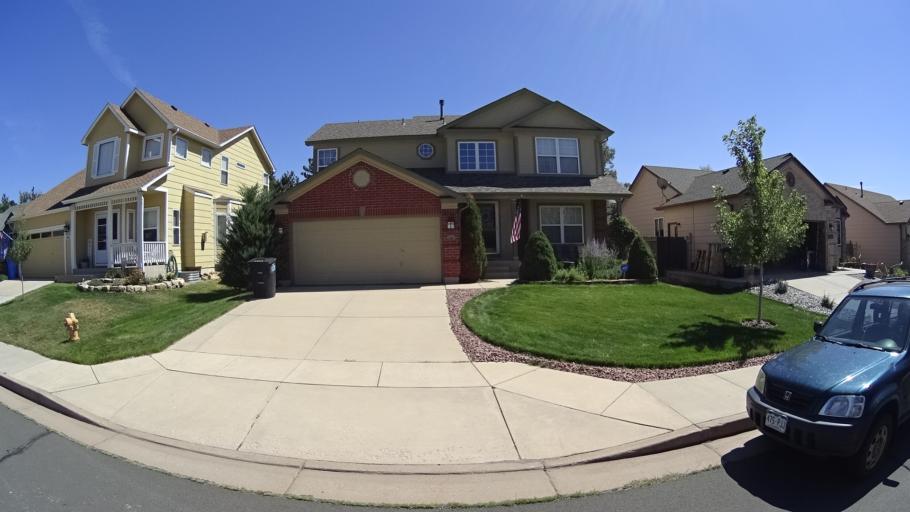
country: US
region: Colorado
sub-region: El Paso County
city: Black Forest
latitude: 38.9502
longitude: -104.7575
